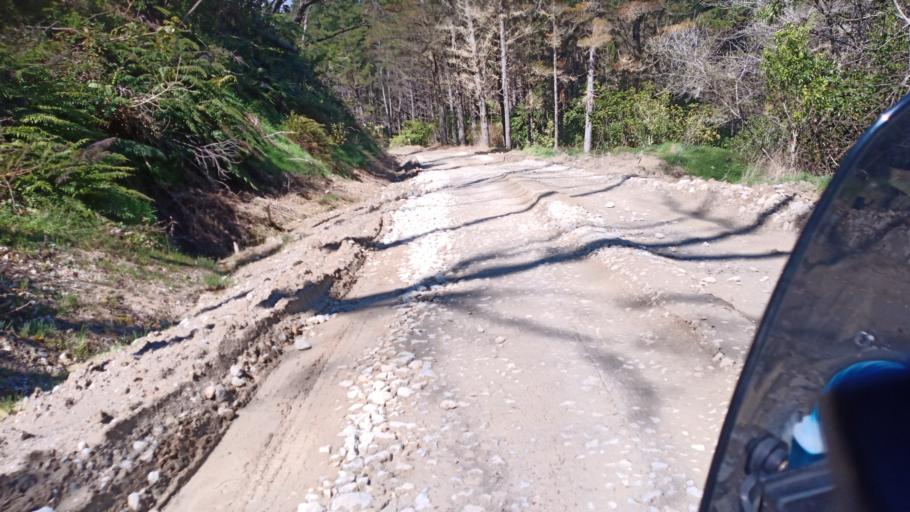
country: NZ
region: Gisborne
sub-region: Gisborne District
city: Gisborne
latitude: -38.8913
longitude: 177.7919
